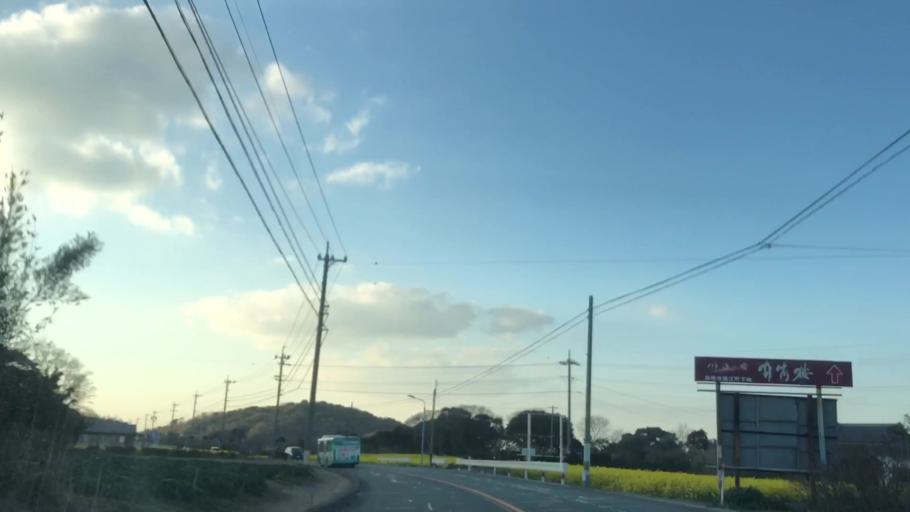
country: JP
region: Aichi
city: Tahara
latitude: 34.6650
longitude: 137.1943
